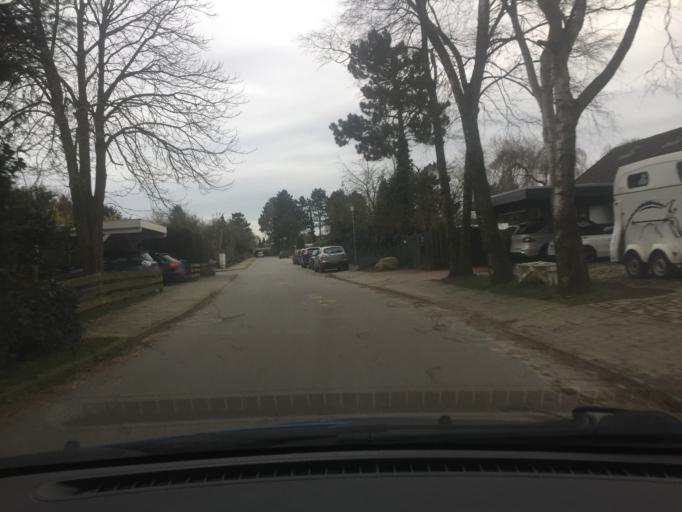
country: DE
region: Lower Saxony
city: Salzhausen
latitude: 53.2253
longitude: 10.1929
